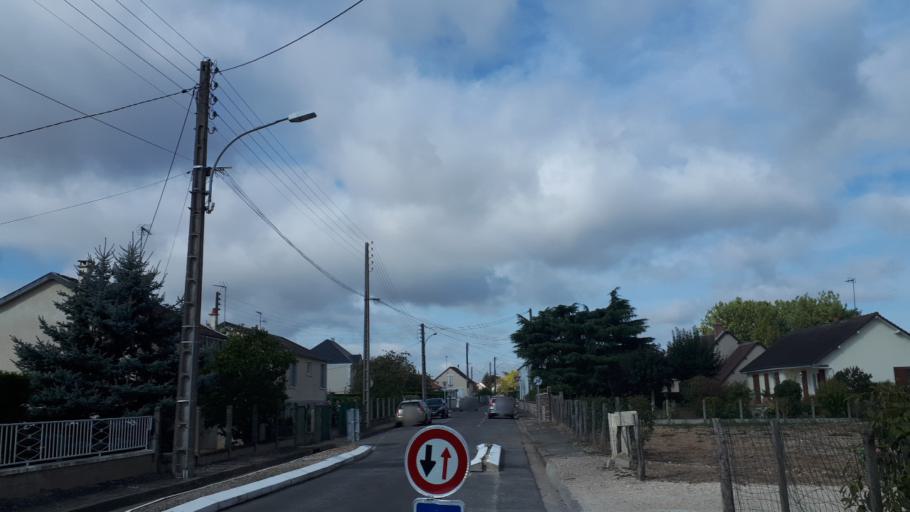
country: FR
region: Centre
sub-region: Departement du Loir-et-Cher
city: Naveil
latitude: 47.7956
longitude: 1.0445
